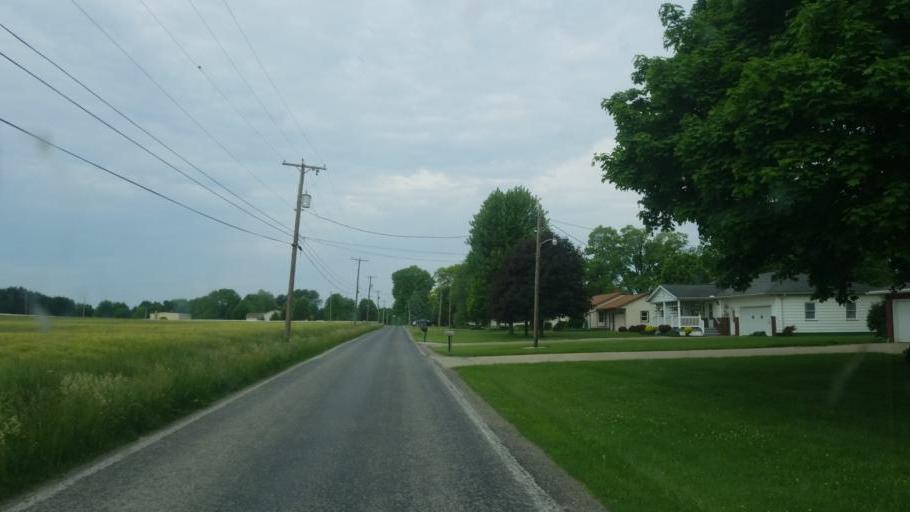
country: US
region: Ohio
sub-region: Wayne County
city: Dalton
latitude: 40.7827
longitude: -81.7494
